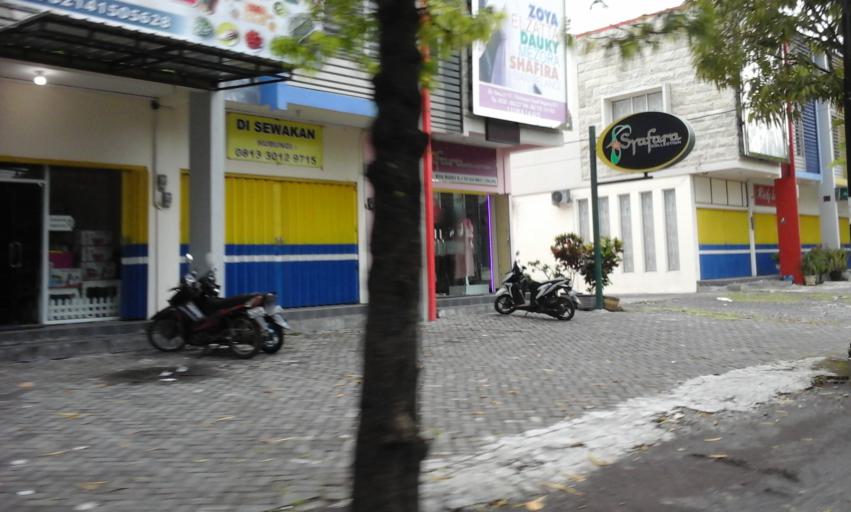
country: ID
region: East Java
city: Rogotrunan
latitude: -8.1194
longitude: 113.2250
